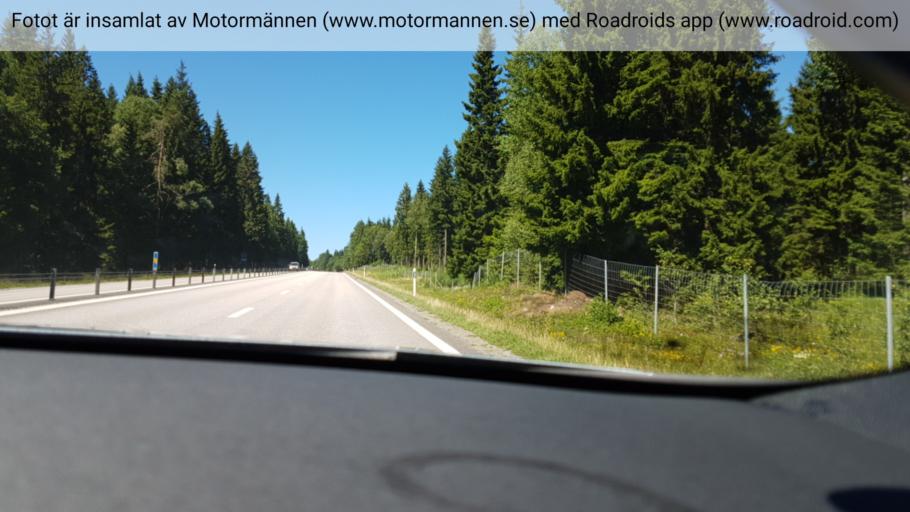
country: SE
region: Vaestra Goetaland
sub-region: Ulricehamns Kommun
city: Ulricehamn
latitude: 57.7981
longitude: 13.5330
